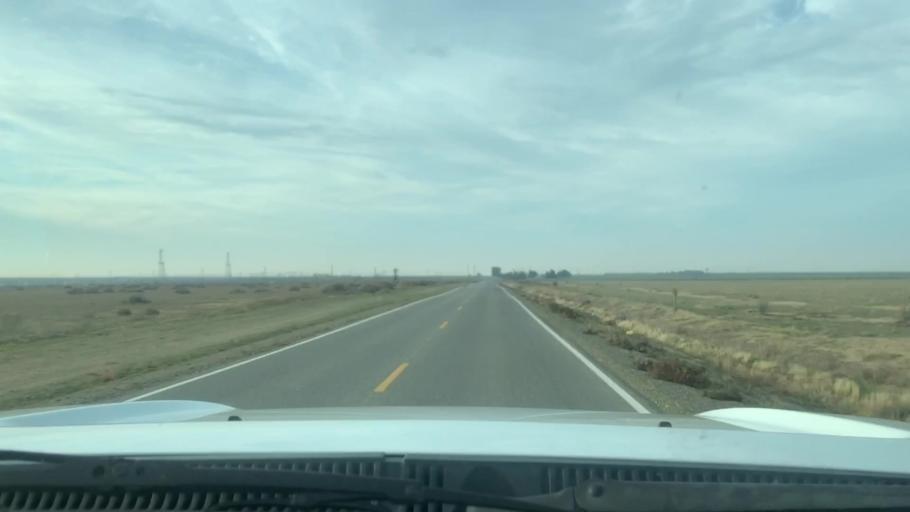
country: US
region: California
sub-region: Kern County
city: Lost Hills
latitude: 35.5305
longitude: -119.7638
